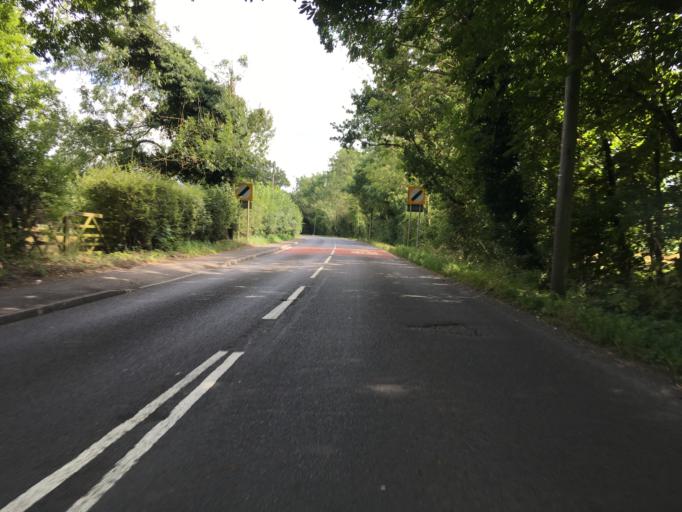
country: GB
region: England
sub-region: Kent
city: Headcorn
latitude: 51.1126
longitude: 0.6432
